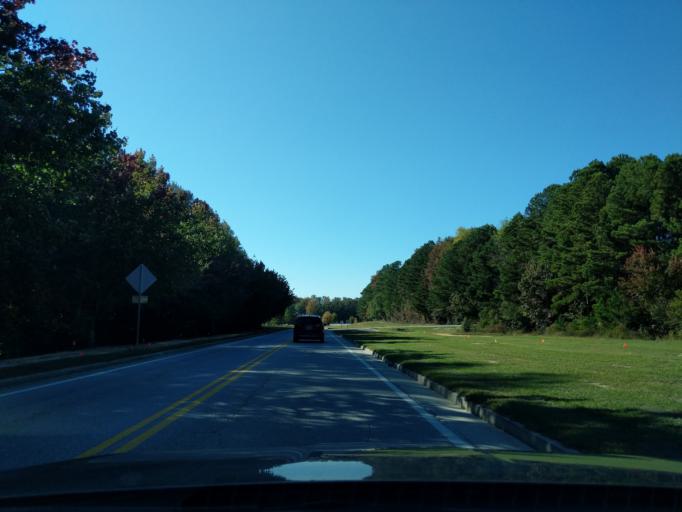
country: US
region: Georgia
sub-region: Columbia County
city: Grovetown
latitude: 33.4664
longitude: -82.1871
